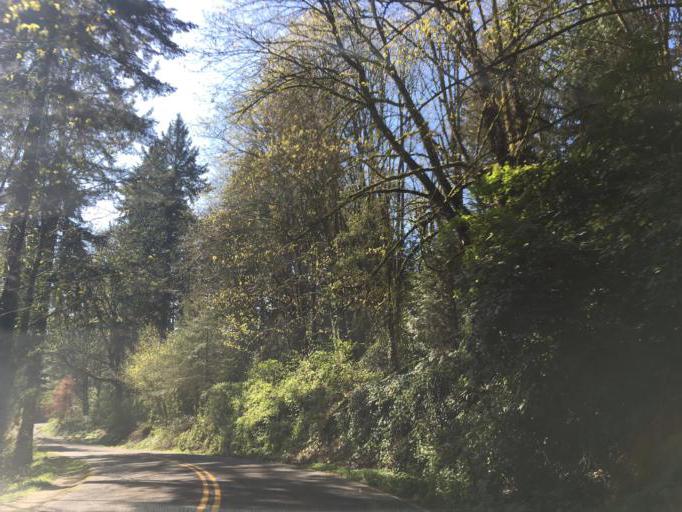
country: US
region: Oregon
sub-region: Multnomah County
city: Portland
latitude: 45.5148
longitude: -122.7061
